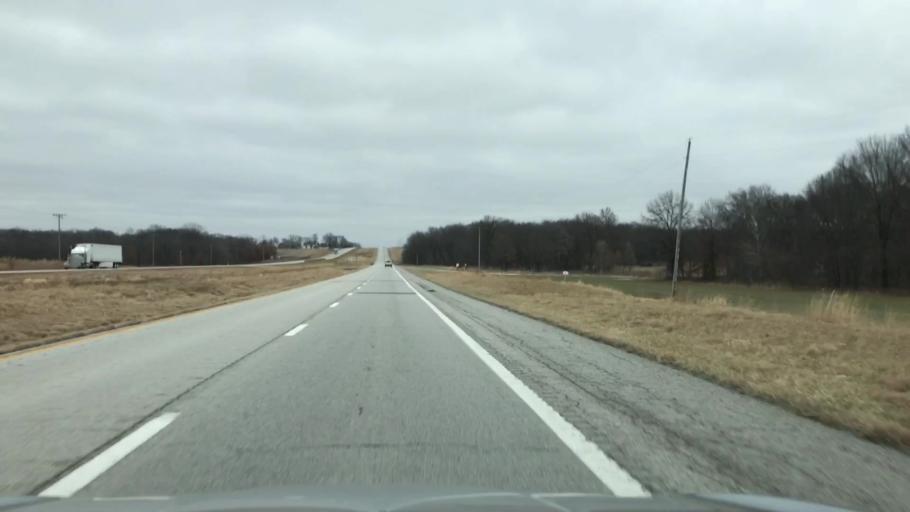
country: US
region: Missouri
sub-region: Linn County
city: Linneus
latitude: 39.7776
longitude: -93.2716
